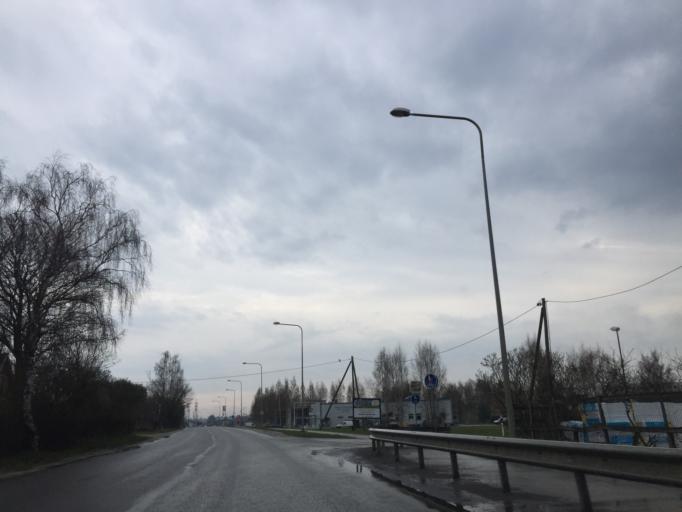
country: EE
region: Tartu
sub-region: UElenurme vald
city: Ulenurme
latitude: 58.3380
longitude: 26.7149
